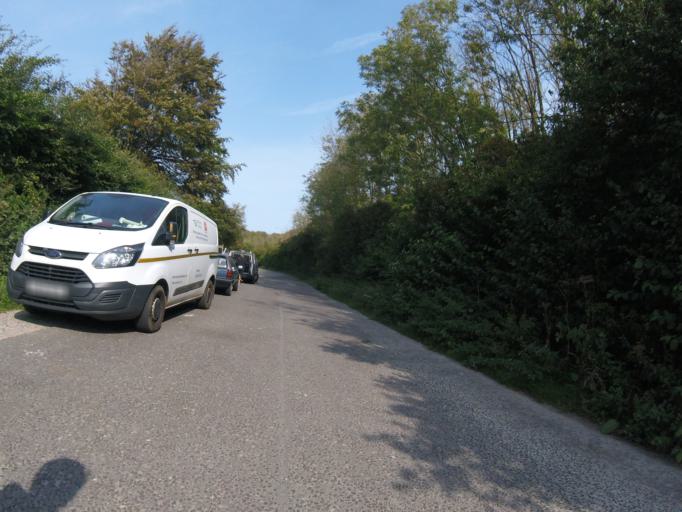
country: GB
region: England
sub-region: Brighton and Hove
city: Hove
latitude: 50.8678
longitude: -0.1598
